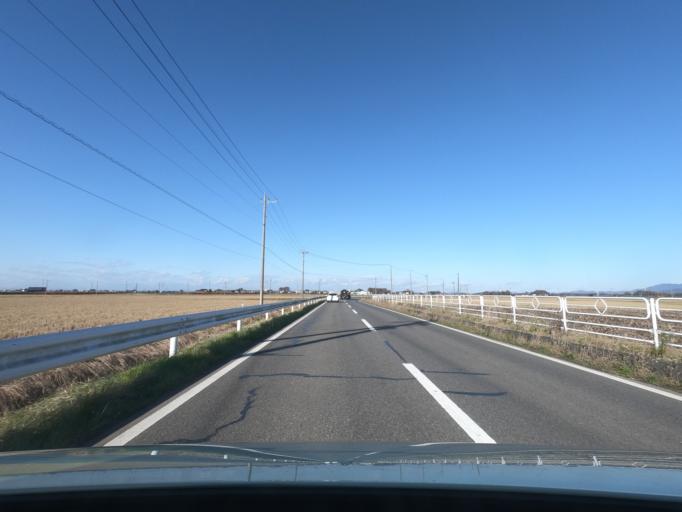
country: JP
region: Ibaraki
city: Ishige
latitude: 36.1529
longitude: 139.9964
